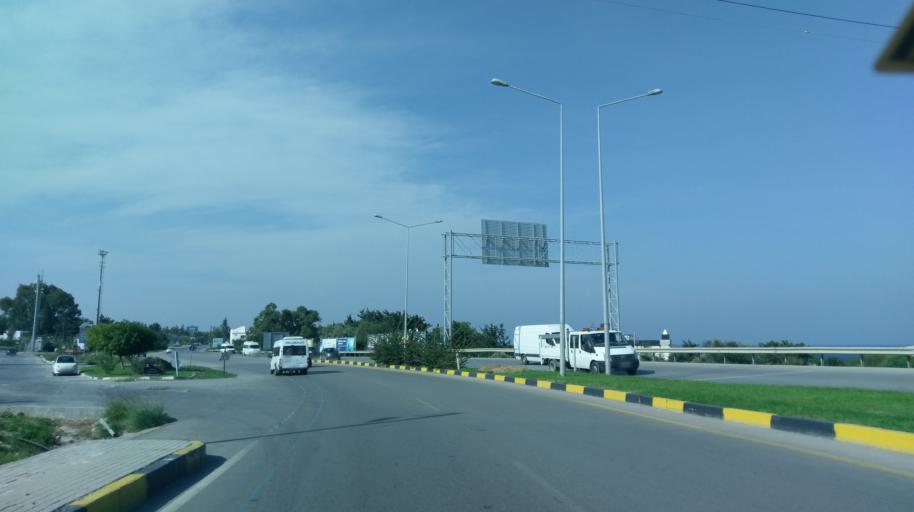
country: CY
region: Keryneia
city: Kyrenia
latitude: 35.3427
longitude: 33.2463
